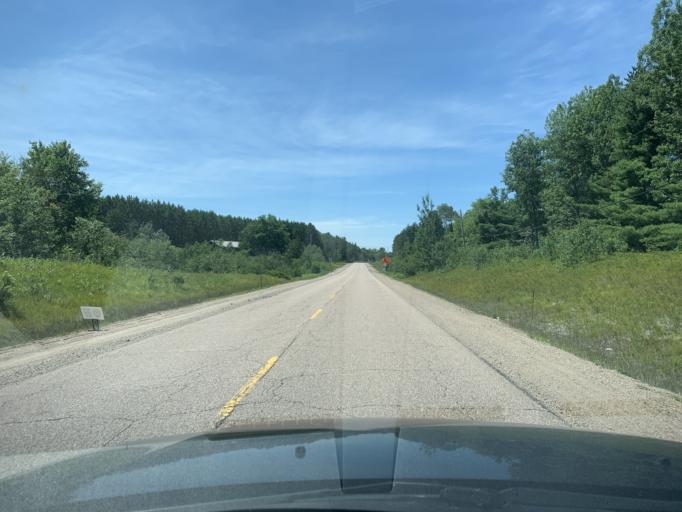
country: CA
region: Ontario
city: Petawawa
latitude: 45.6678
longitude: -77.5664
